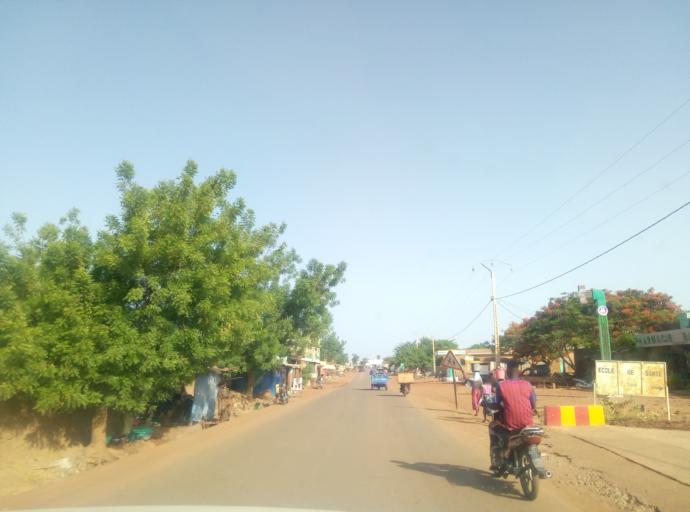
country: ML
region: Bamako
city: Bamako
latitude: 12.6117
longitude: -7.7757
